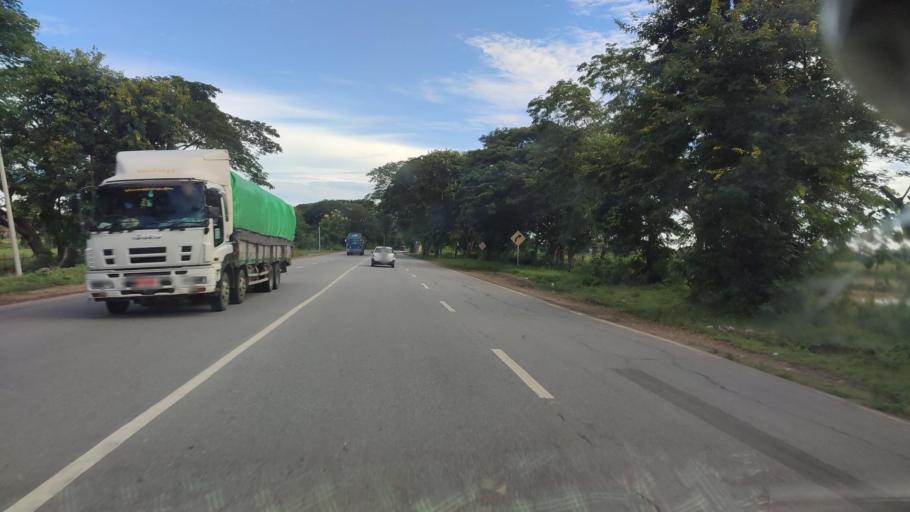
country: MM
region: Mandalay
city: Yamethin
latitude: 20.2312
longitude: 96.1793
